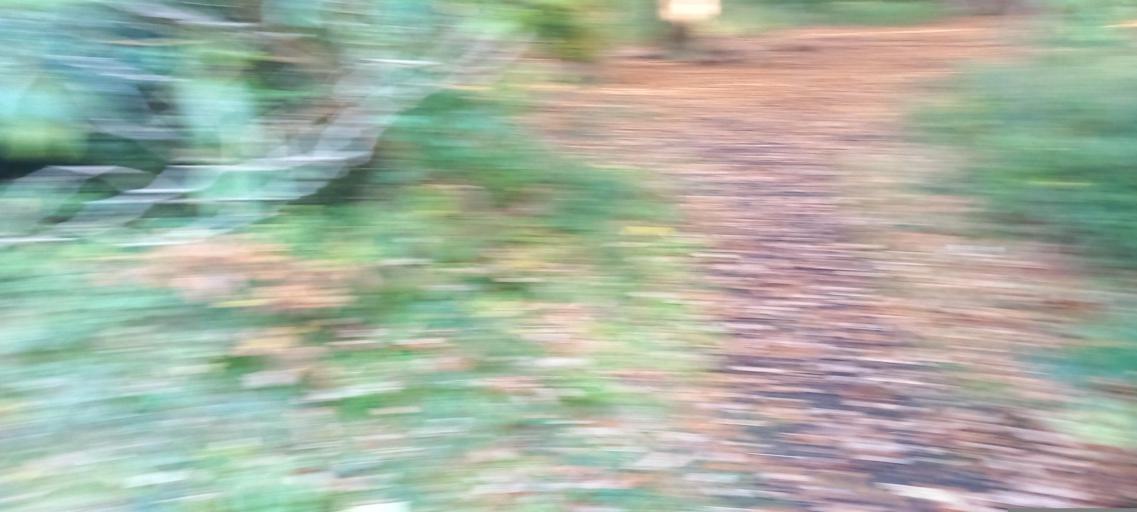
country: GB
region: Wales
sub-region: Gwynedd
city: Bangor
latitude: 53.2262
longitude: -4.0976
